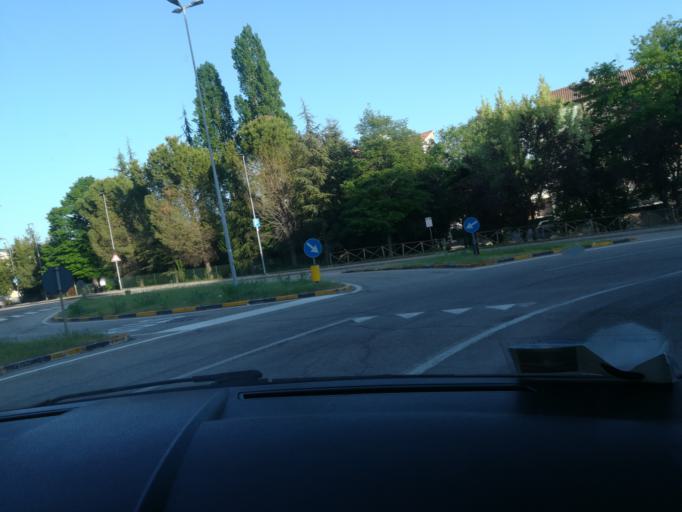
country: IT
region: The Marches
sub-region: Provincia di Macerata
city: Macerata
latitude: 43.2908
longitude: 13.4339
